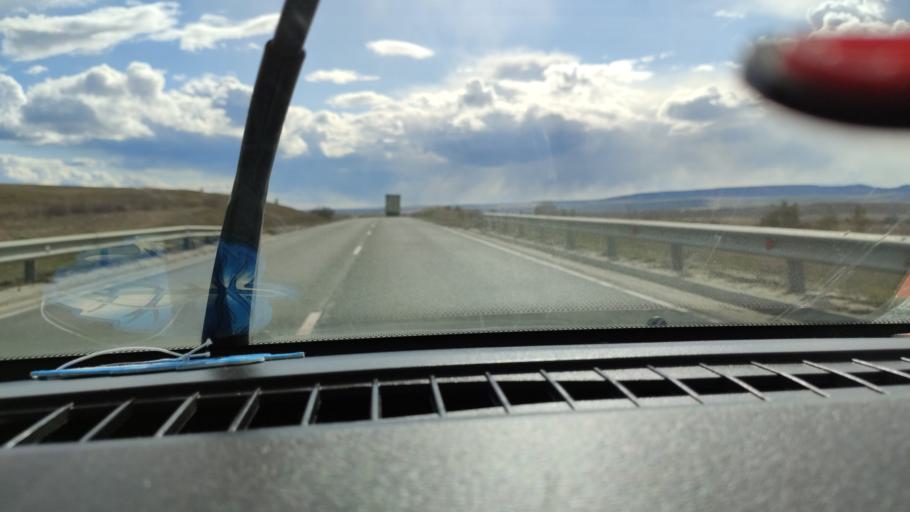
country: RU
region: Saratov
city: Alekseyevka
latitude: 52.3540
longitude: 47.9438
